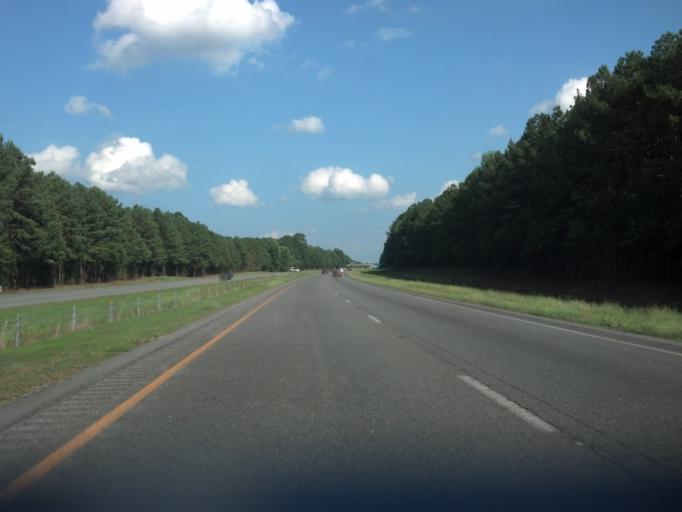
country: US
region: North Carolina
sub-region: Nash County
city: Rocky Mount
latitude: 35.9350
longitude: -77.7226
